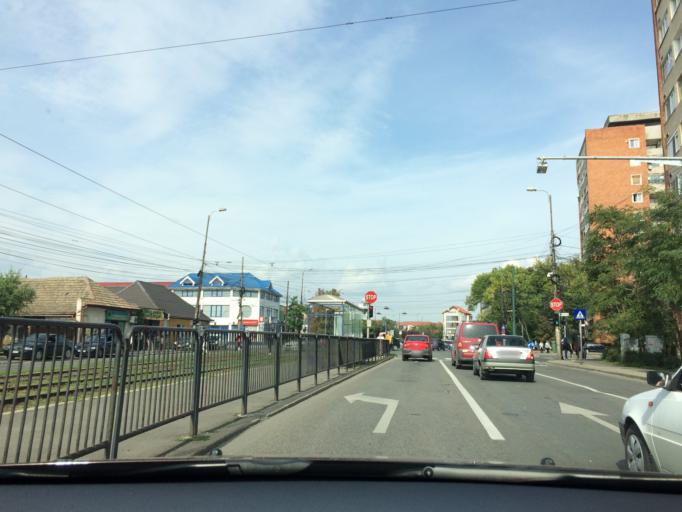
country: RO
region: Timis
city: Timisoara
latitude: 45.7623
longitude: 21.2104
